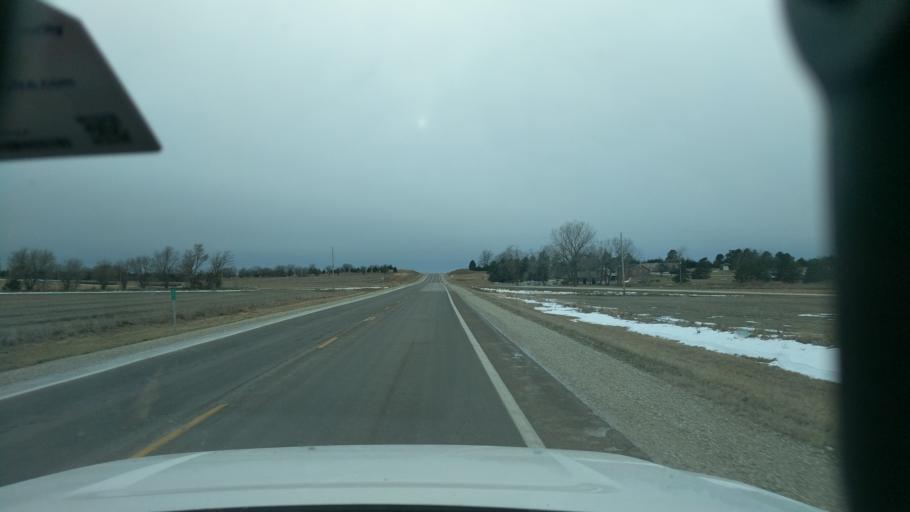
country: US
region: Kansas
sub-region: Dickinson County
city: Herington
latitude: 38.6510
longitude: -96.9380
